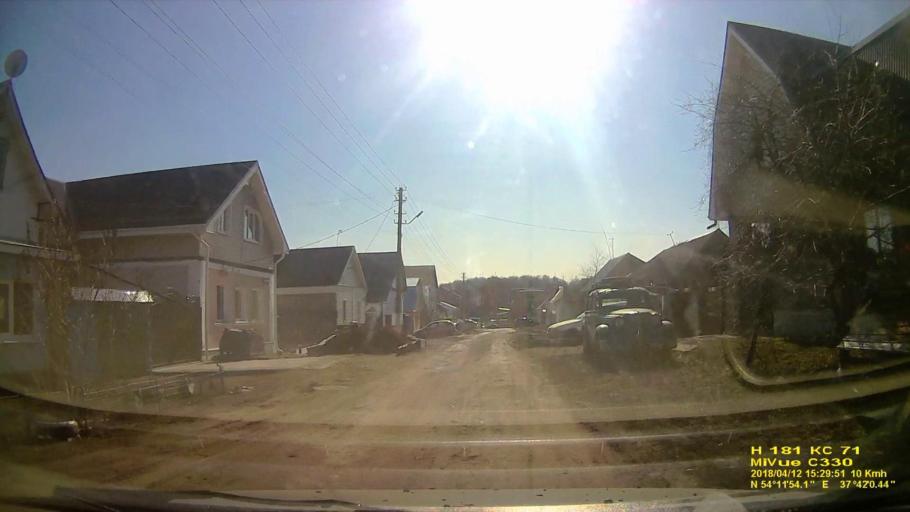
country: RU
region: Tula
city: Tula
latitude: 54.1983
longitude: 37.7001
